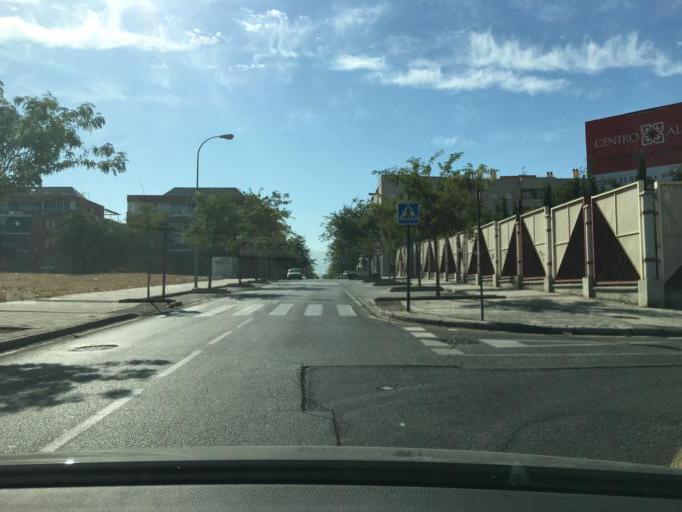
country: ES
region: Andalusia
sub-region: Provincia de Granada
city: Maracena
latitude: 37.2094
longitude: -3.6197
